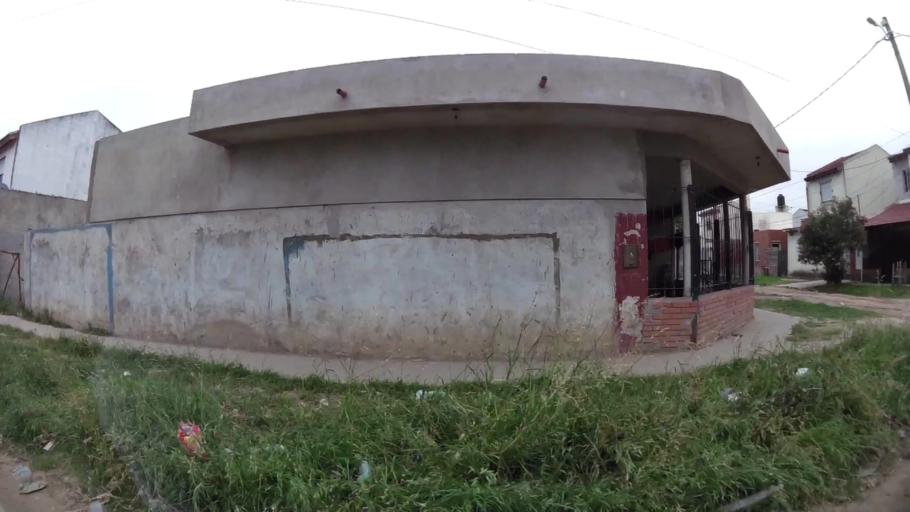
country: AR
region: Buenos Aires
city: San Justo
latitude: -34.6988
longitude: -58.5466
